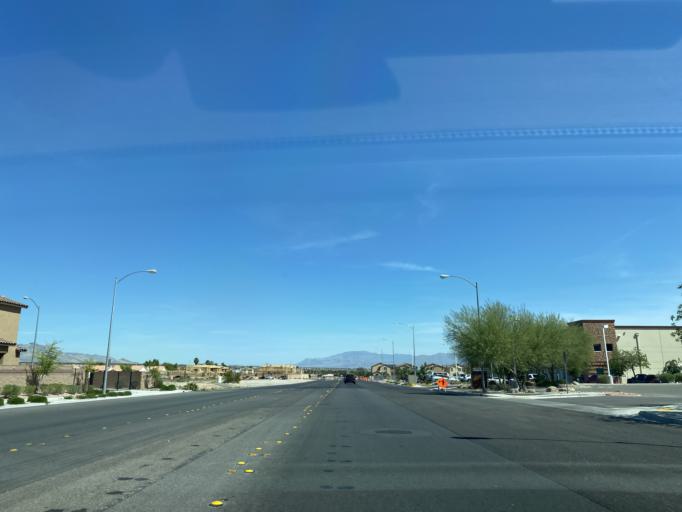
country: US
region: Nevada
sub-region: Clark County
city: Spring Valley
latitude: 36.0788
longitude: -115.2608
